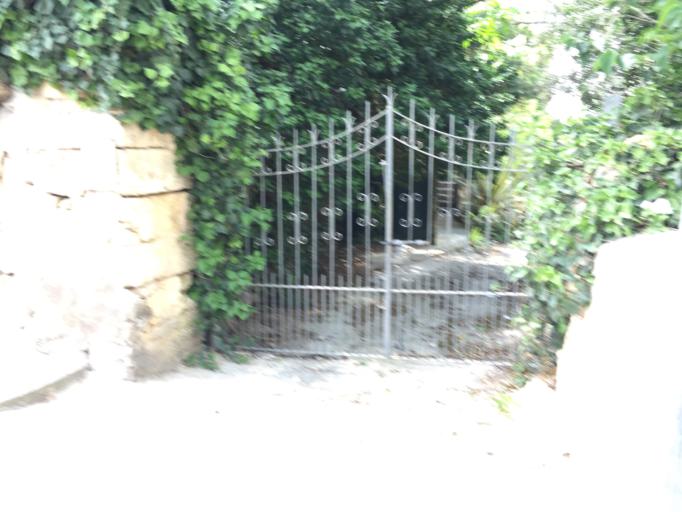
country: MT
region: Dingli
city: Dingli
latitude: 35.8637
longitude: 14.3849
